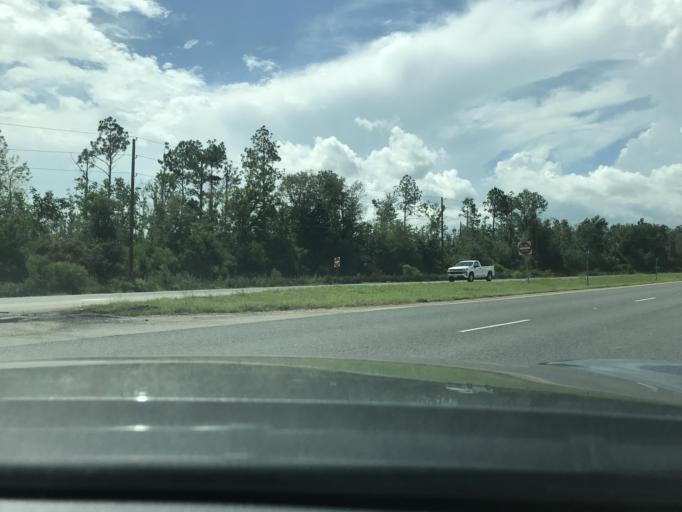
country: US
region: Louisiana
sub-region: Calcasieu Parish
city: Moss Bluff
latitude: 30.3444
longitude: -93.2005
